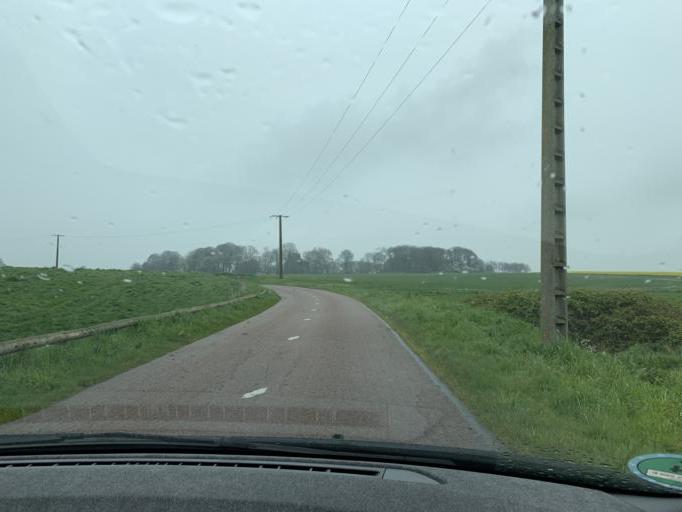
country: FR
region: Haute-Normandie
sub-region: Departement de la Seine-Maritime
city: Les Loges
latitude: 49.7188
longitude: 0.2761
